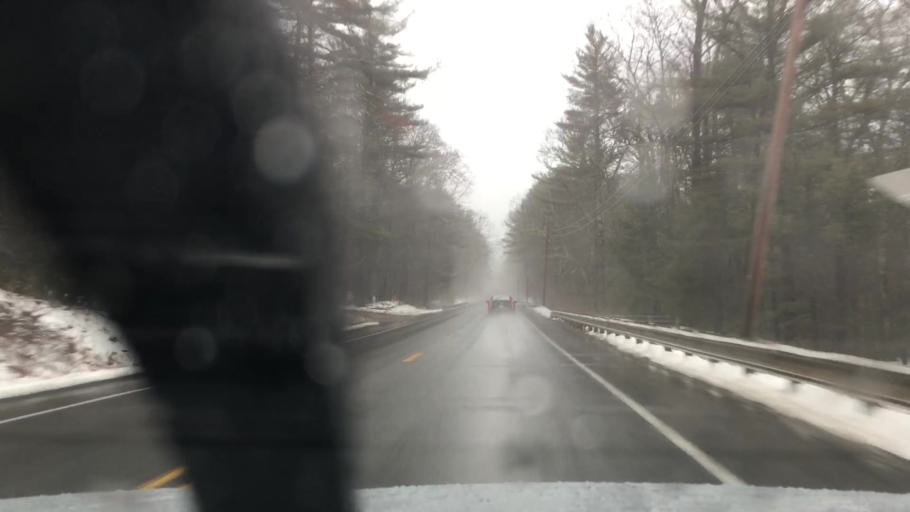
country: US
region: Massachusetts
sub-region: Franklin County
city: Orange
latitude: 42.5232
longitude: -72.3235
